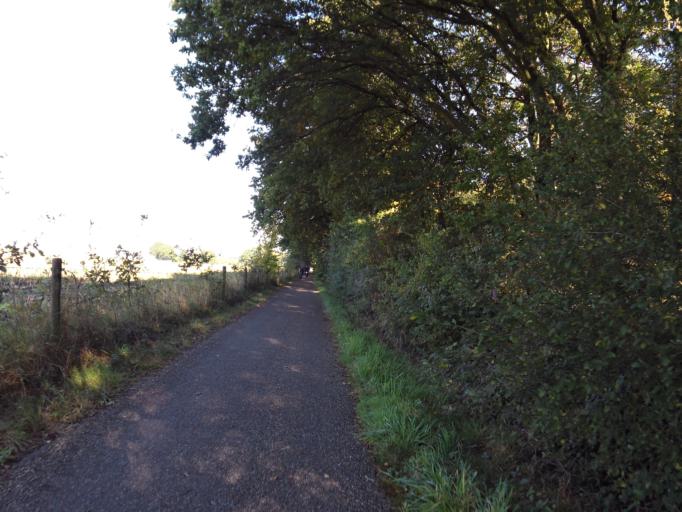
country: NL
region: Limburg
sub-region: Gemeente Venlo
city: Venlo
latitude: 51.4188
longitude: 6.2035
